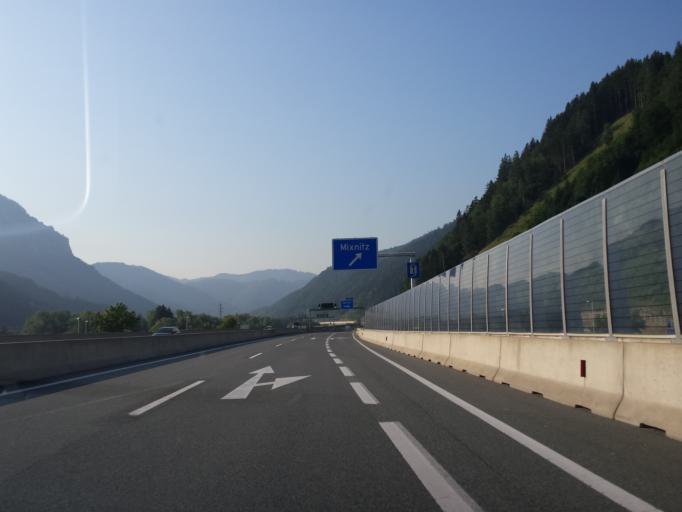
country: AT
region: Styria
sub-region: Politischer Bezirk Bruck-Muerzzuschlag
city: Pernegg an der Mur
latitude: 47.3433
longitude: 15.3487
